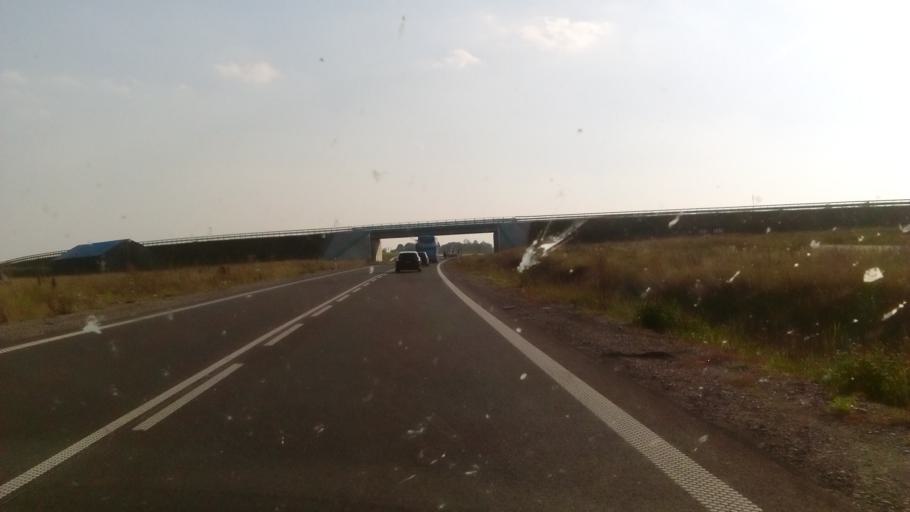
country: PL
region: Podlasie
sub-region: Powiat grajewski
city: Rajgrod
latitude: 53.7666
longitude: 22.8313
